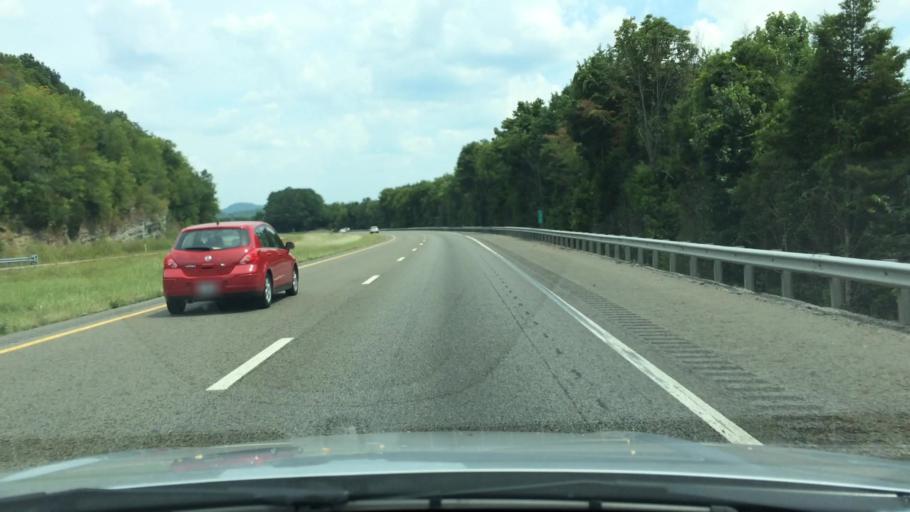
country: US
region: Tennessee
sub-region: Marshall County
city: Cornersville
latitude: 35.4125
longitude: -86.8773
